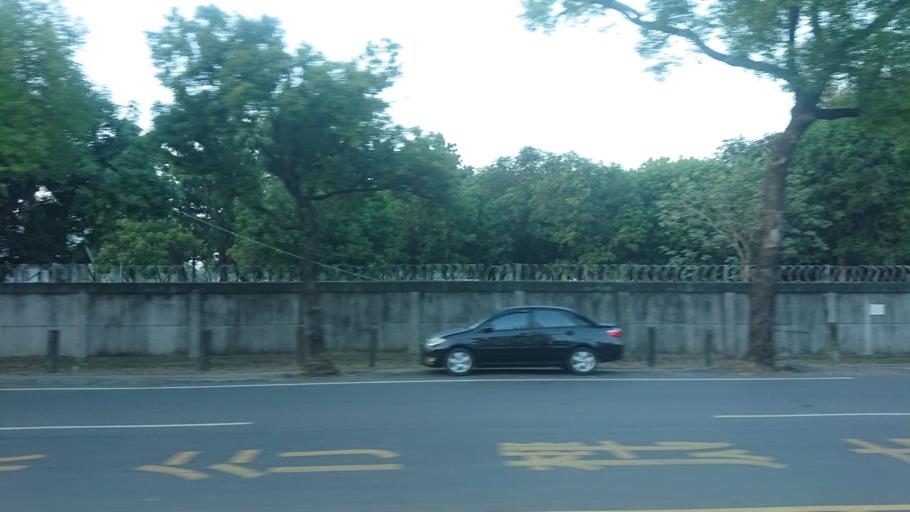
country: TW
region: Taiwan
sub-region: Tainan
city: Tainan
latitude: 23.0201
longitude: 120.2438
